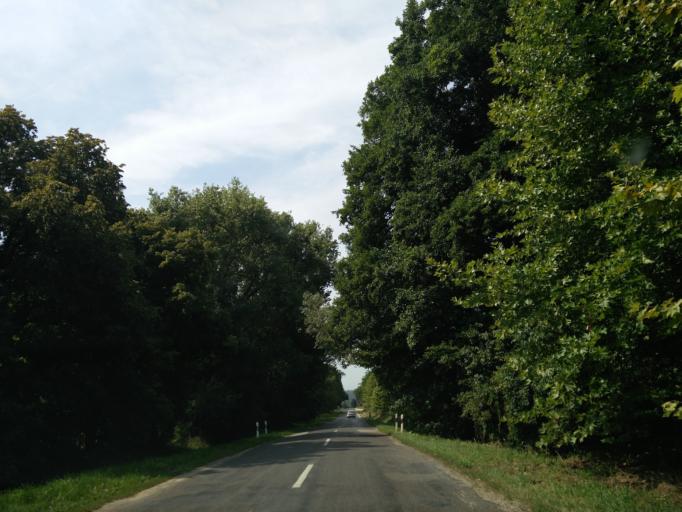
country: HU
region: Fejer
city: Bicske
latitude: 47.4344
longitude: 18.6063
